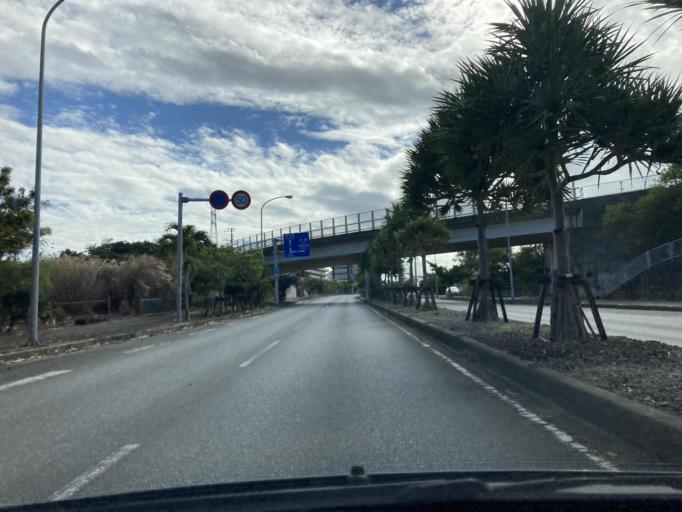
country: JP
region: Okinawa
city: Tomigusuku
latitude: 26.1666
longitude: 127.7256
